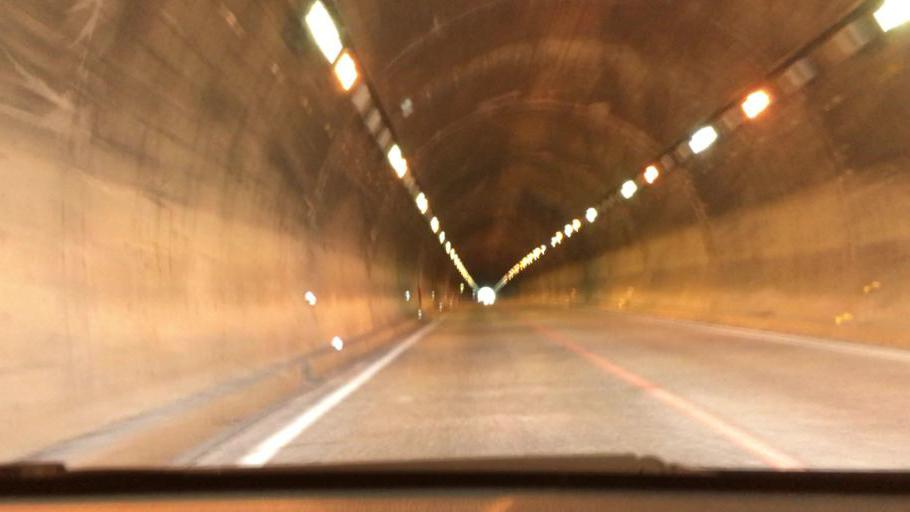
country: JP
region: Yamaguchi
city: Tokuyama
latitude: 34.0611
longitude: 131.8352
